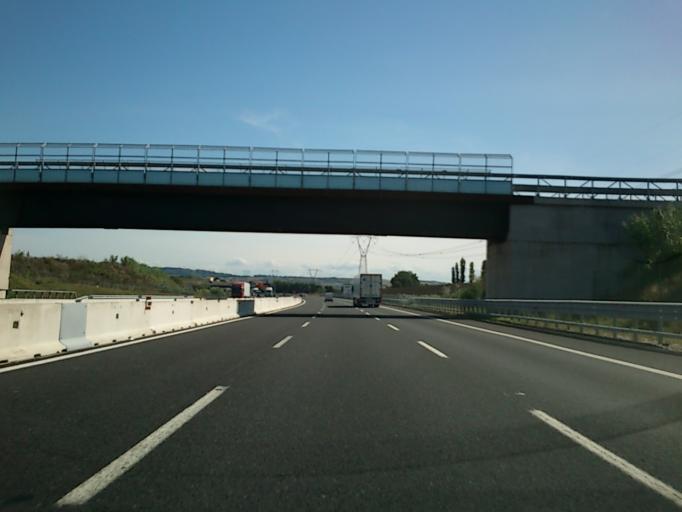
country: IT
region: The Marches
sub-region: Provincia di Pesaro e Urbino
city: Borgo Santa Maria
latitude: 43.9102
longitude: 12.8211
